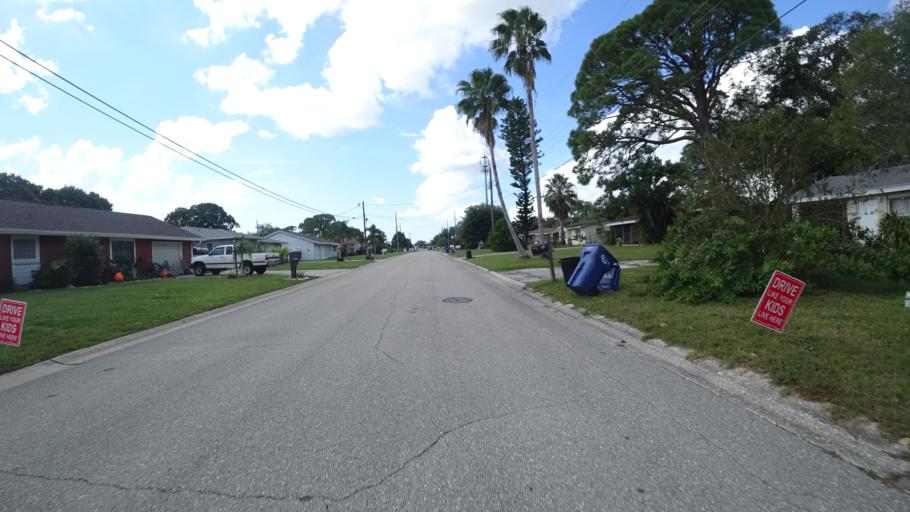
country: US
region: Florida
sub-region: Manatee County
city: Whitfield
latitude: 27.4203
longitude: -82.5722
